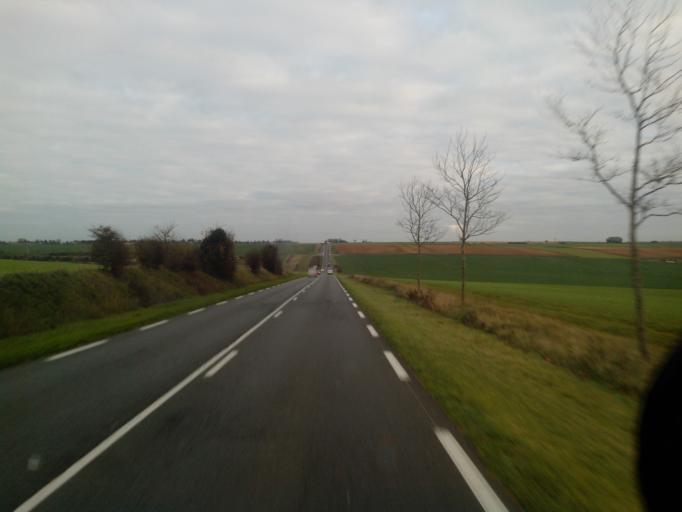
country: FR
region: Poitou-Charentes
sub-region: Departement de la Vienne
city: Cisse
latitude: 46.6381
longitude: 0.2140
